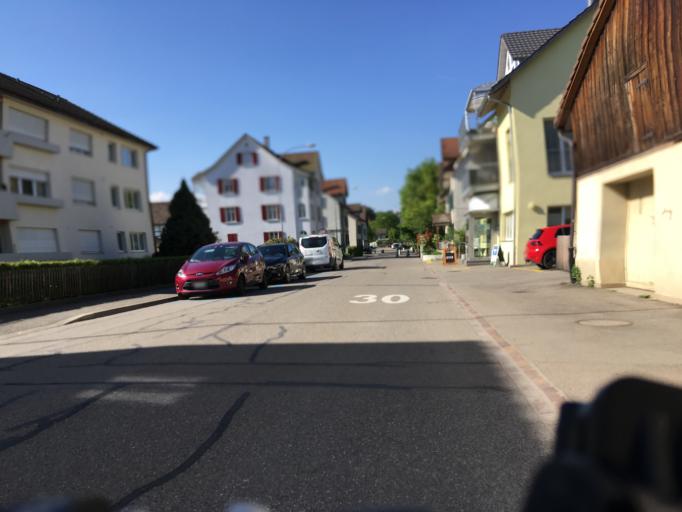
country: CH
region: Zurich
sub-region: Bezirk Andelfingen
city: Flurlingen
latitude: 47.6850
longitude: 8.6276
